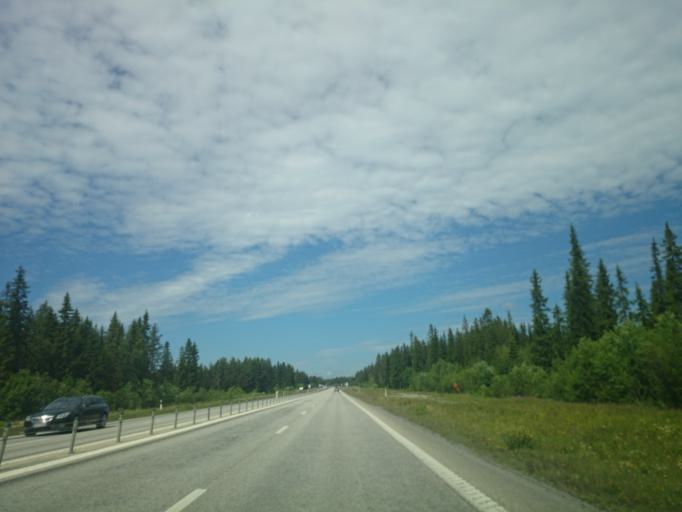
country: SE
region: Jaemtland
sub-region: OEstersunds Kommun
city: Brunflo
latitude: 63.1334
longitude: 14.7896
